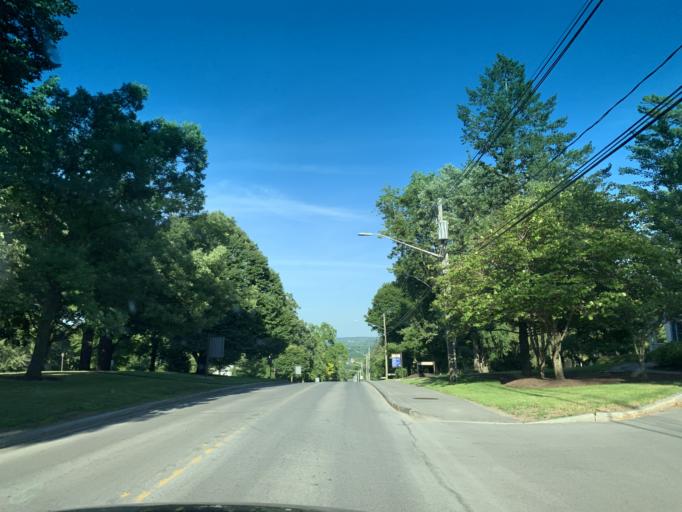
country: US
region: New York
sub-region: Oneida County
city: Clinton
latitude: 43.0504
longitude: -75.4059
